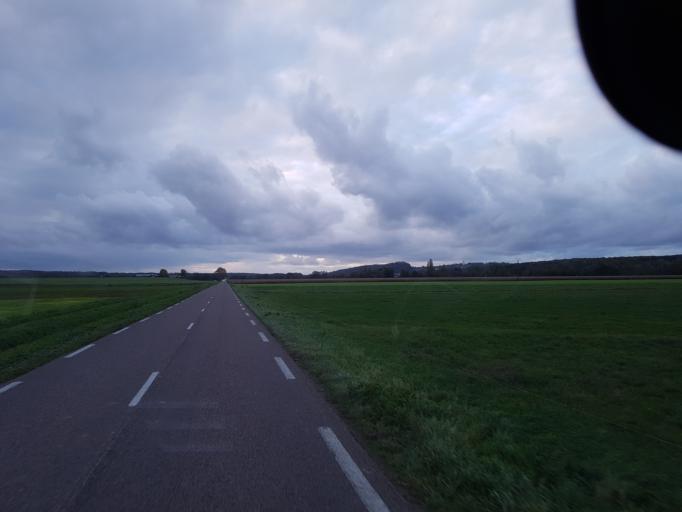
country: FR
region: Franche-Comte
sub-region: Departement du Jura
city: Arbois
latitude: 46.9180
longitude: 5.7360
